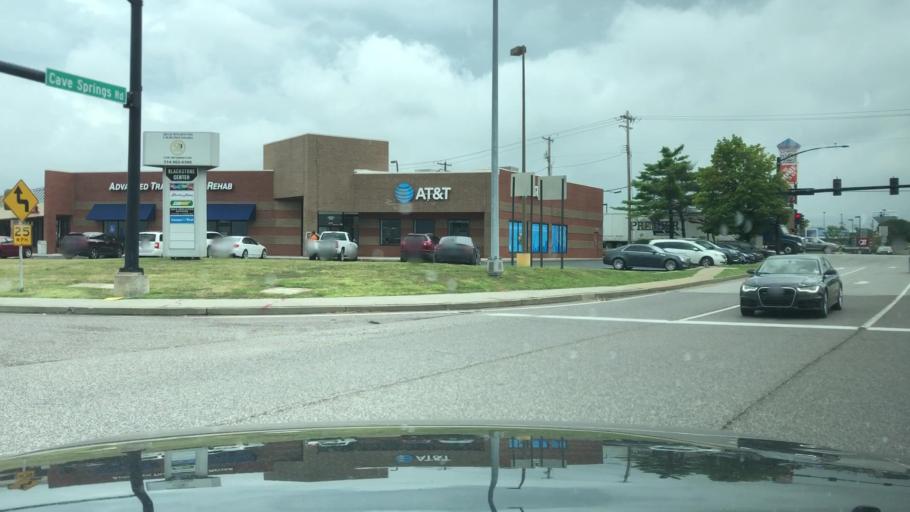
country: US
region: Missouri
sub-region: Saint Charles County
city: Saint Peters
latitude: 38.7918
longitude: -90.5658
